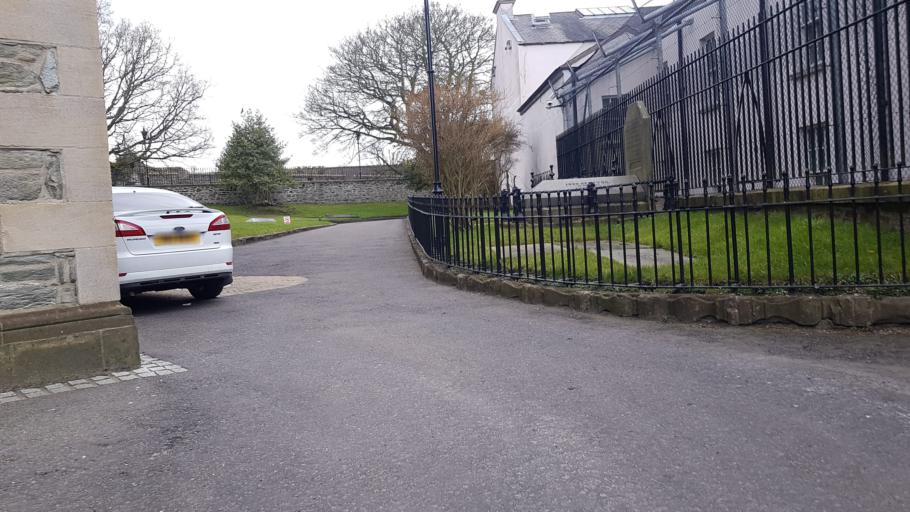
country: GB
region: Northern Ireland
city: Londonderry County Borough
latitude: 54.9940
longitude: -7.3234
